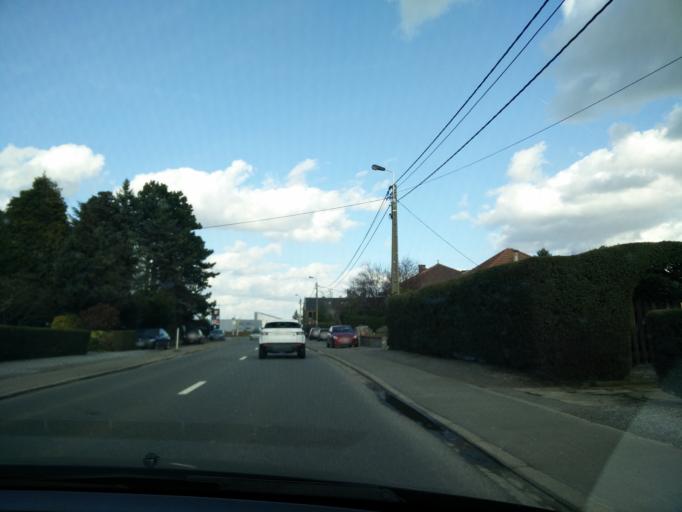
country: BE
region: Wallonia
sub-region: Province de Liege
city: Vise
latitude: 50.7381
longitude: 5.7102
